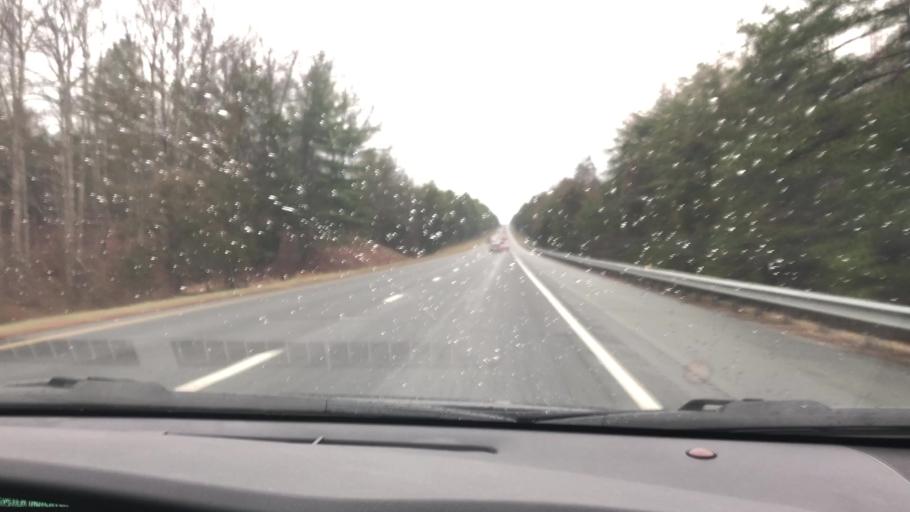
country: US
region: Virginia
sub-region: Fluvanna County
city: Palmyra
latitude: 37.9630
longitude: -78.1779
